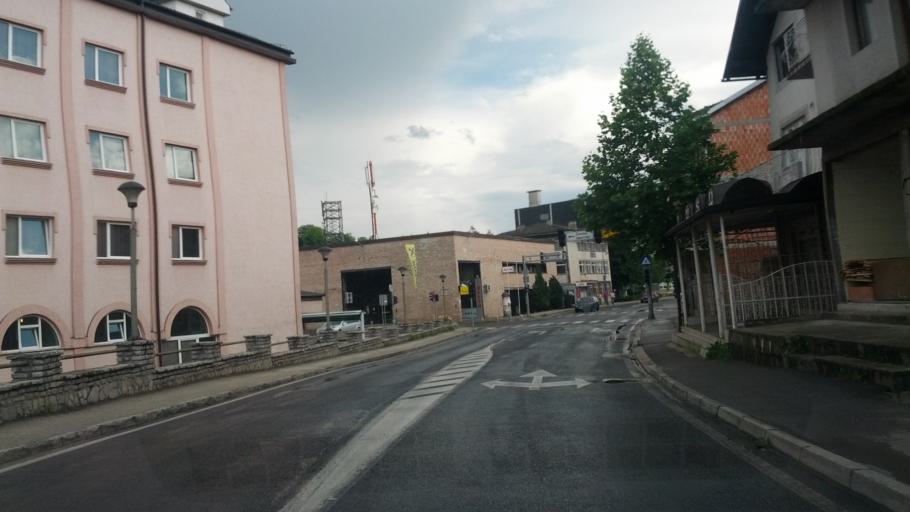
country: BA
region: Federation of Bosnia and Herzegovina
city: Bosanska Krupa
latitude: 44.8848
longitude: 16.1532
